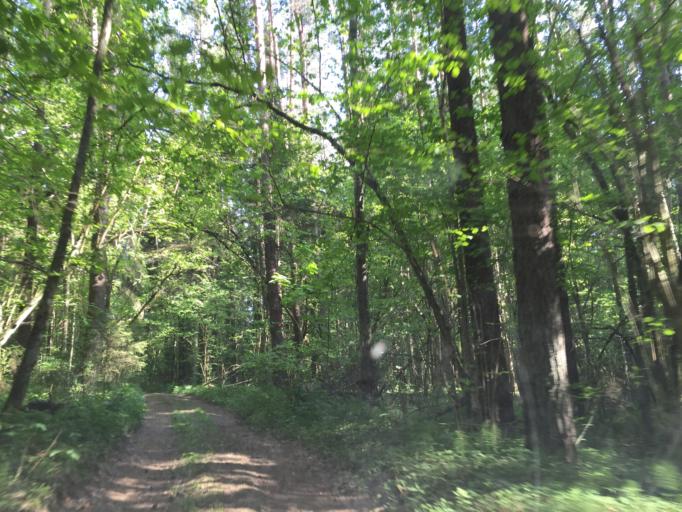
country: LV
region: Baldone
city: Baldone
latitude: 56.7981
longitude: 24.3743
